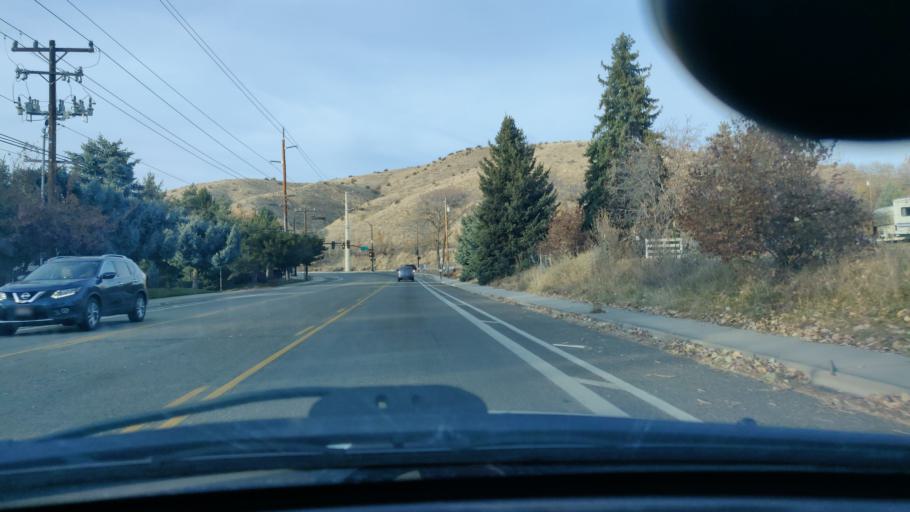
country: US
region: Idaho
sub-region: Ada County
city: Garden City
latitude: 43.6827
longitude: -116.2792
